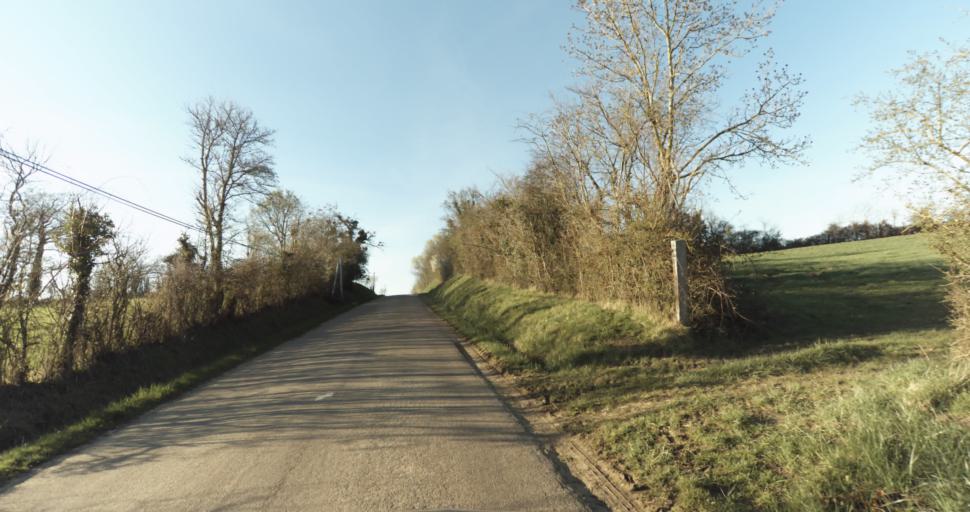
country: FR
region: Lower Normandy
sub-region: Departement du Calvados
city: Saint-Pierre-sur-Dives
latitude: 48.9420
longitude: 0.0185
